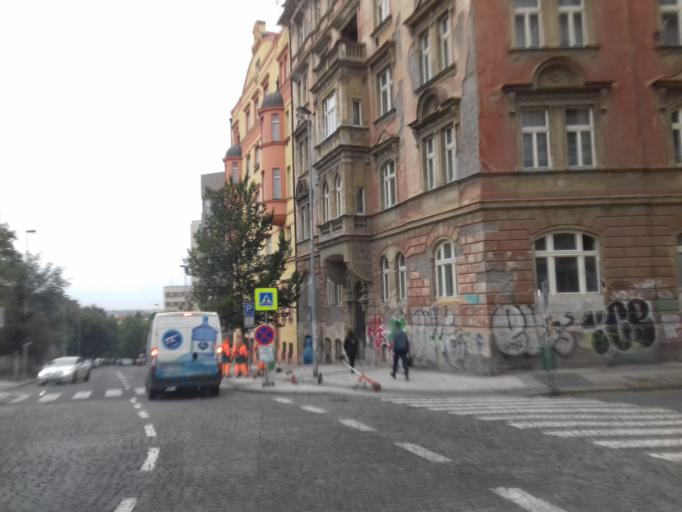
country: CZ
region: Praha
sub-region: Praha 8
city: Karlin
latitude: 50.0826
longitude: 14.4440
